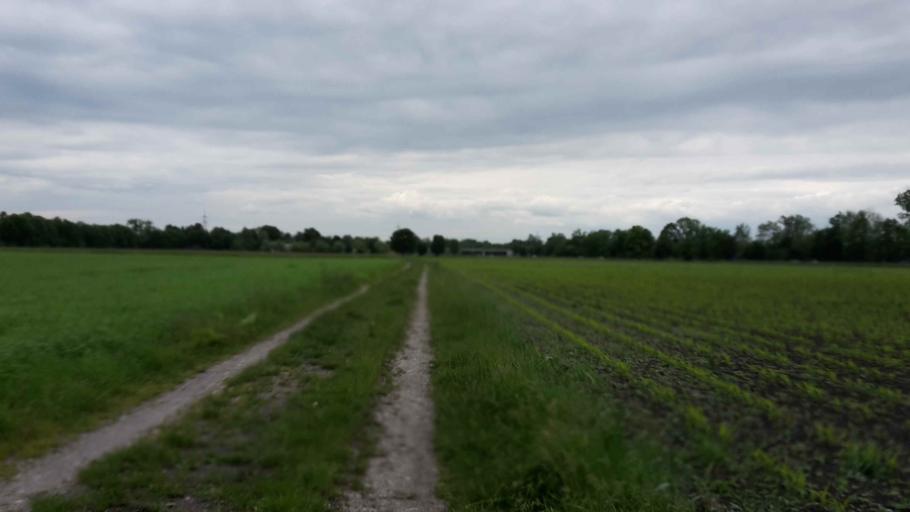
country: DE
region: Bavaria
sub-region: Upper Bavaria
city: Grobenzell
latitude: 48.1909
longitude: 11.4139
